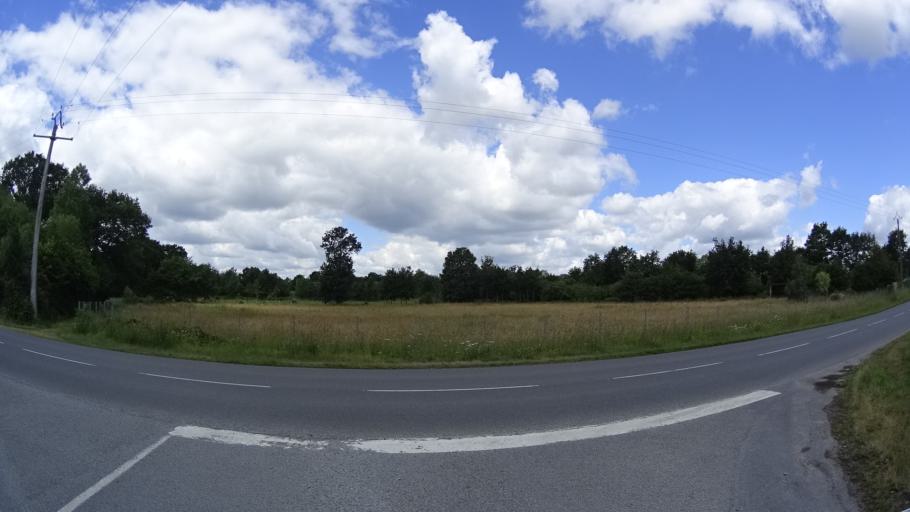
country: FR
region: Brittany
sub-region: Departement d'Ille-et-Vilaine
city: Saint-Gilles
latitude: 48.1316
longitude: -1.8263
